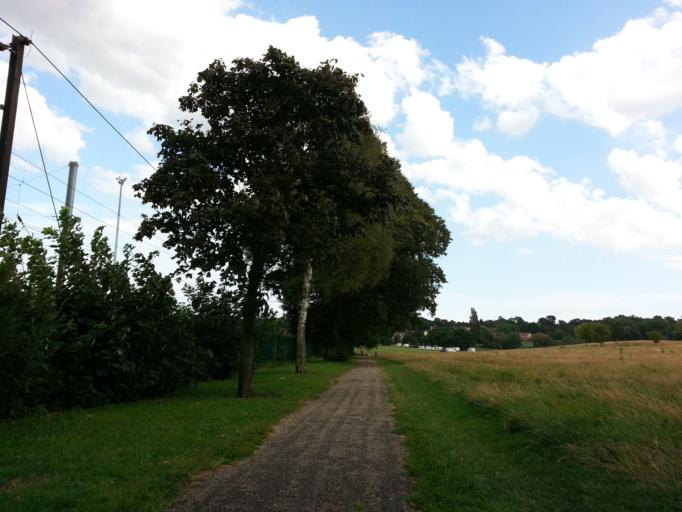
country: GB
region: England
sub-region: Suffolk
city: Ipswich
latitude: 52.0538
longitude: 1.1329
